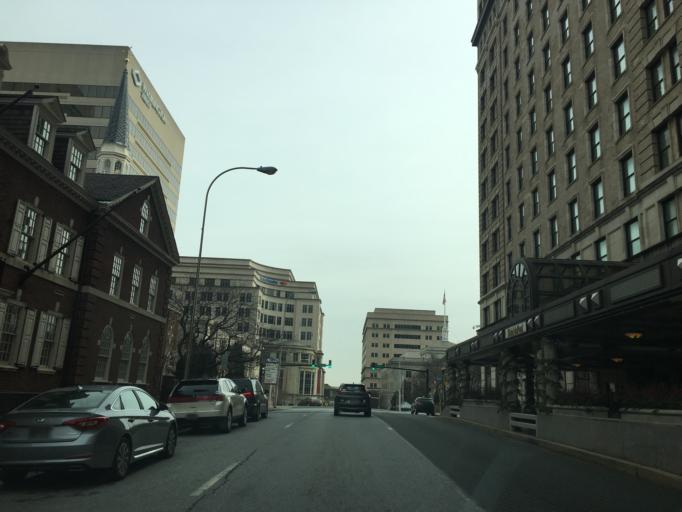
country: US
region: Delaware
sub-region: New Castle County
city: Wilmington
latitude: 39.7467
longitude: -75.5480
